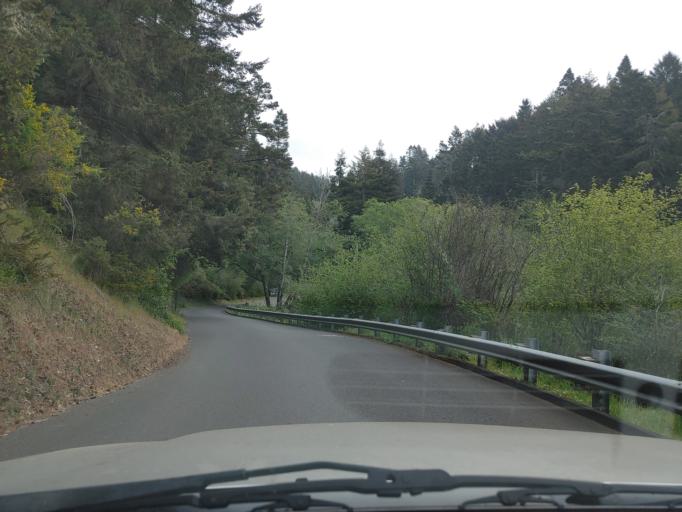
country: US
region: California
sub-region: Mendocino County
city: Fort Bragg
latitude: 39.3302
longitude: -123.8032
